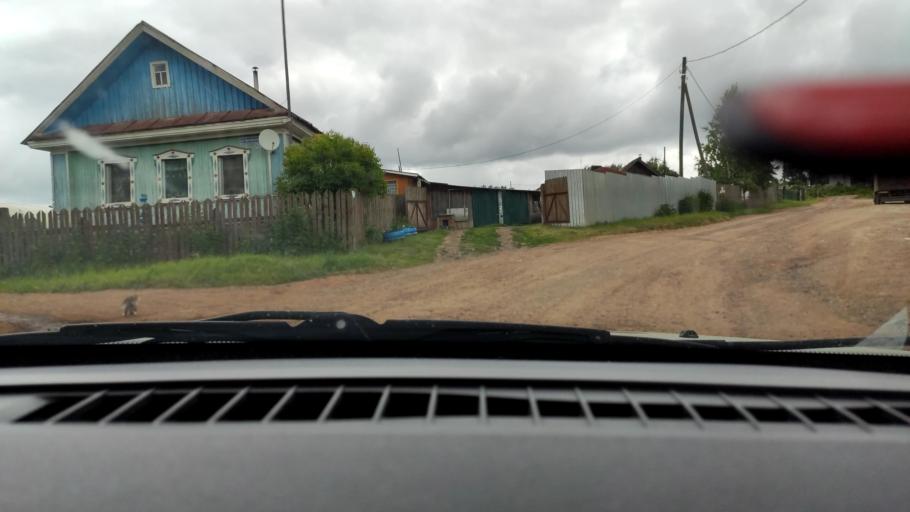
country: RU
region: Perm
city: Chaykovskaya
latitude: 58.1444
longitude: 55.5684
